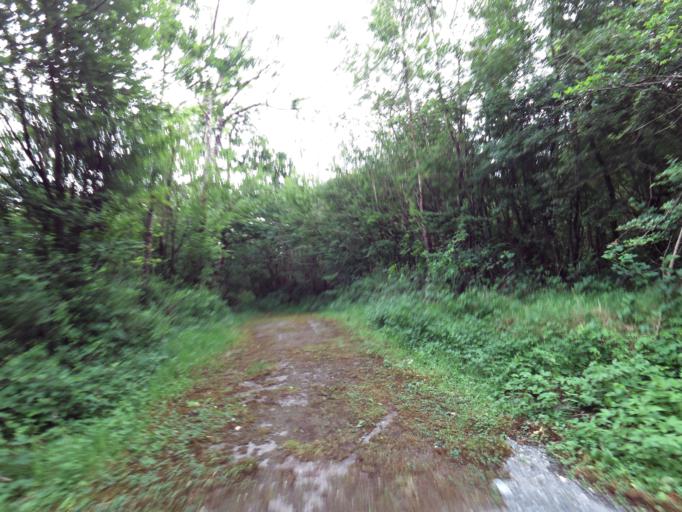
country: IE
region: Connaught
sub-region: County Galway
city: Gort
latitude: 53.0754
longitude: -8.8595
